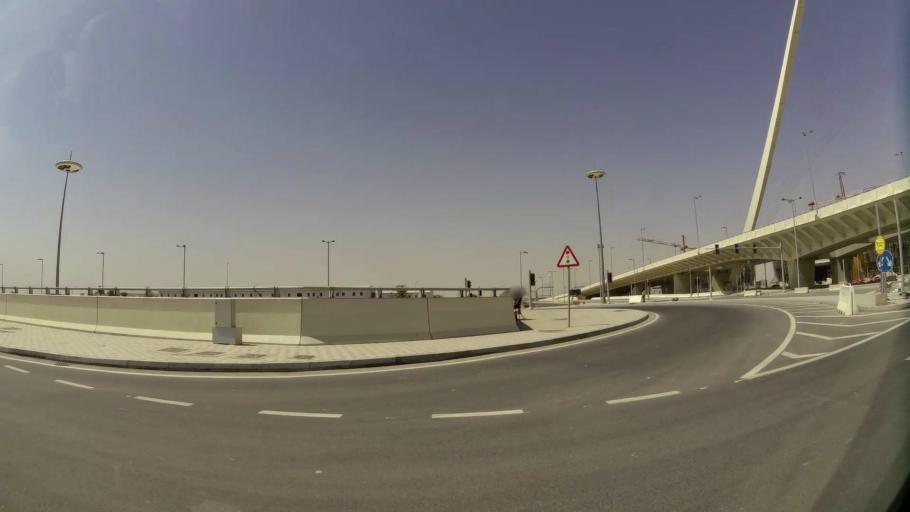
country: QA
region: Baladiyat Umm Salal
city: Umm Salal Muhammad
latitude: 25.4001
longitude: 51.5150
